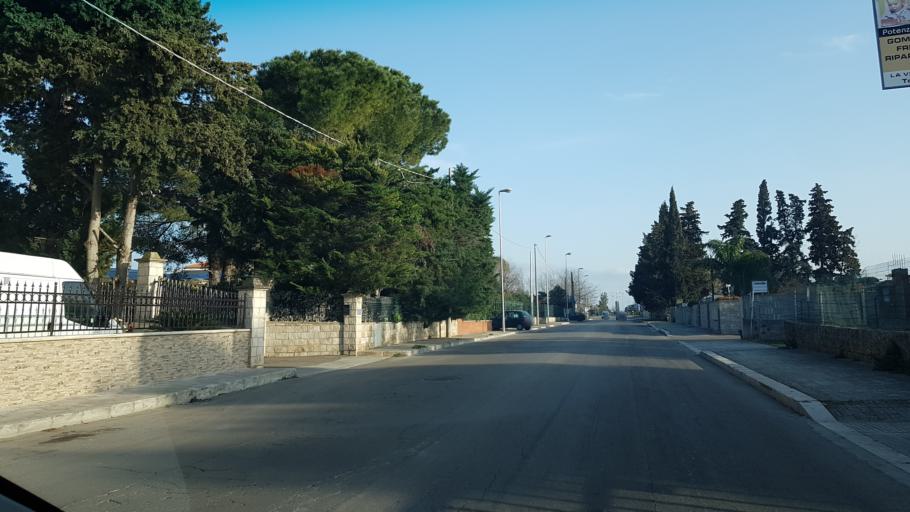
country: IT
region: Apulia
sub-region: Provincia di Lecce
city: Squinzano
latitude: 40.4298
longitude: 18.0512
